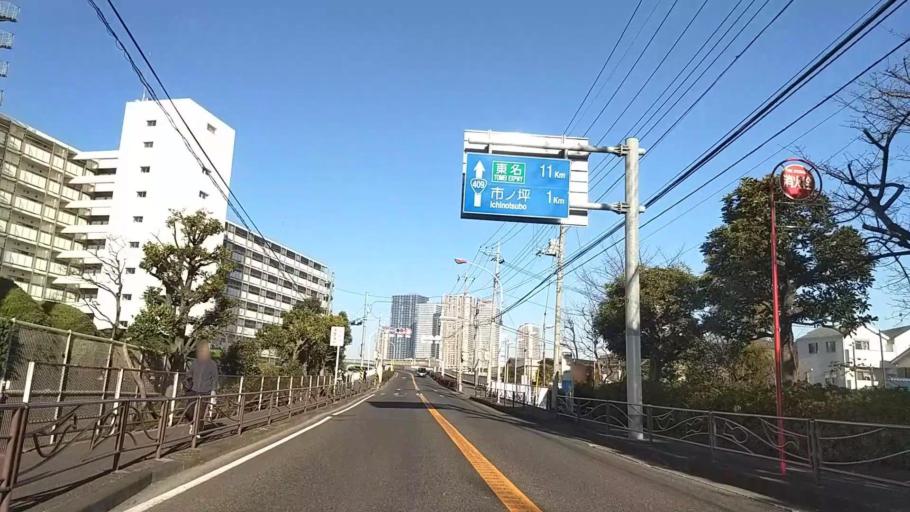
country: JP
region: Kanagawa
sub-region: Kawasaki-shi
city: Kawasaki
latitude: 35.5625
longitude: 139.6684
